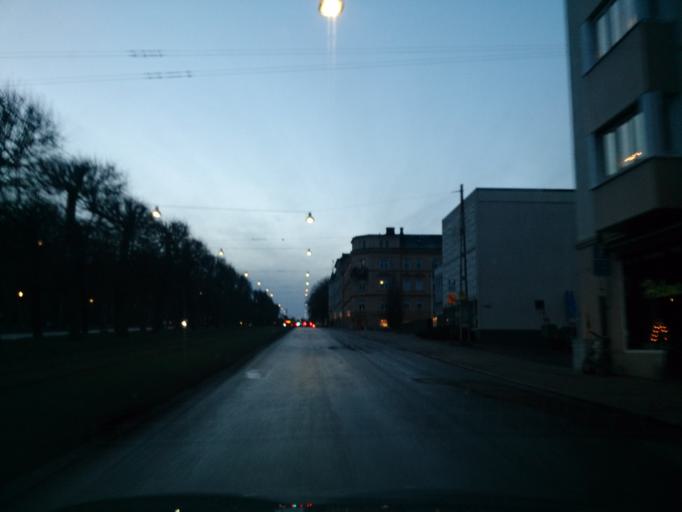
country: SE
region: OEstergoetland
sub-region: Norrkopings Kommun
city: Norrkoping
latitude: 58.5947
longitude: 16.1737
